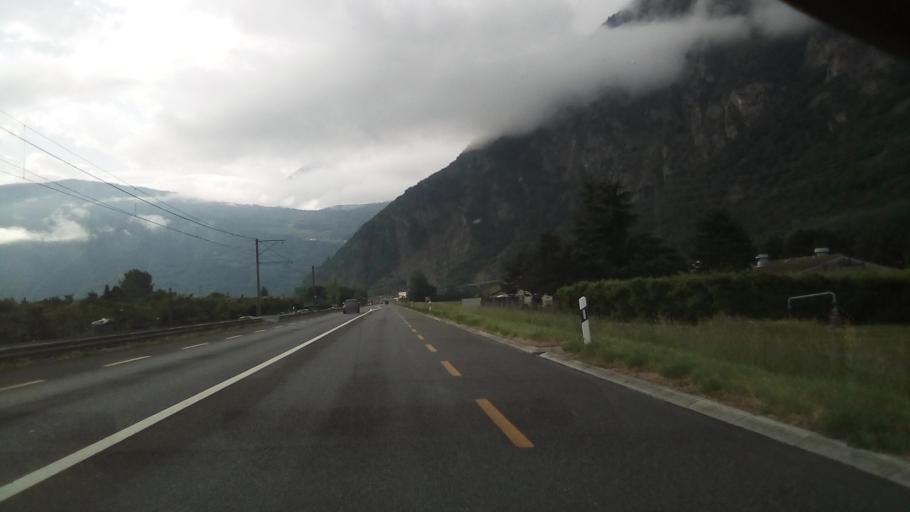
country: CH
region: Valais
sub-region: Saint-Maurice District
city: Vernayaz
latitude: 46.1211
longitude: 7.0517
